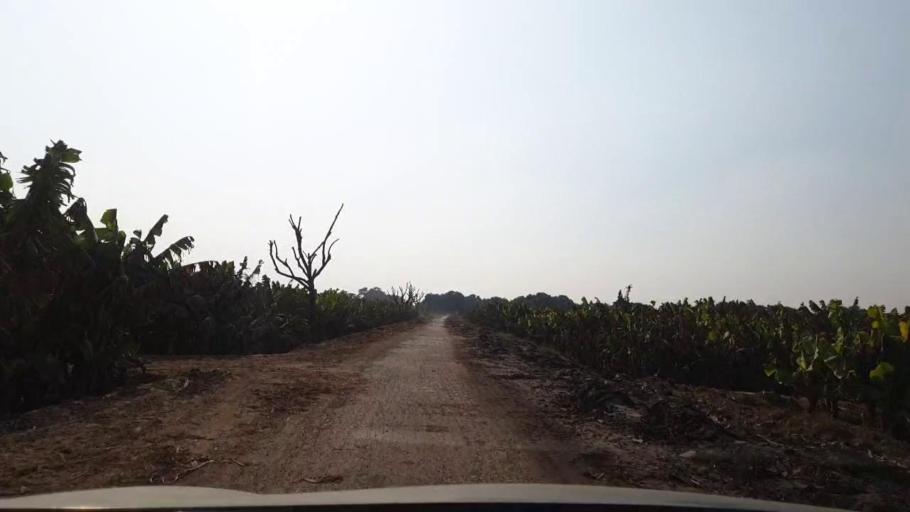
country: PK
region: Sindh
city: Tando Allahyar
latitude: 25.5483
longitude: 68.7732
